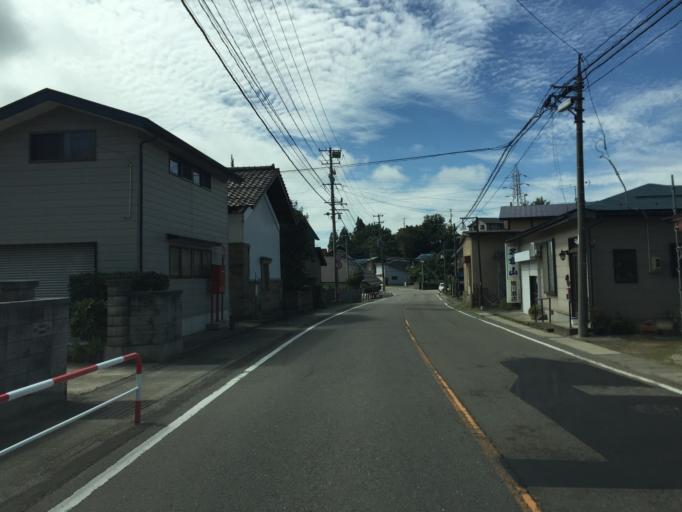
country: JP
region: Fukushima
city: Inawashiro
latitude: 37.5578
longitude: 139.9847
